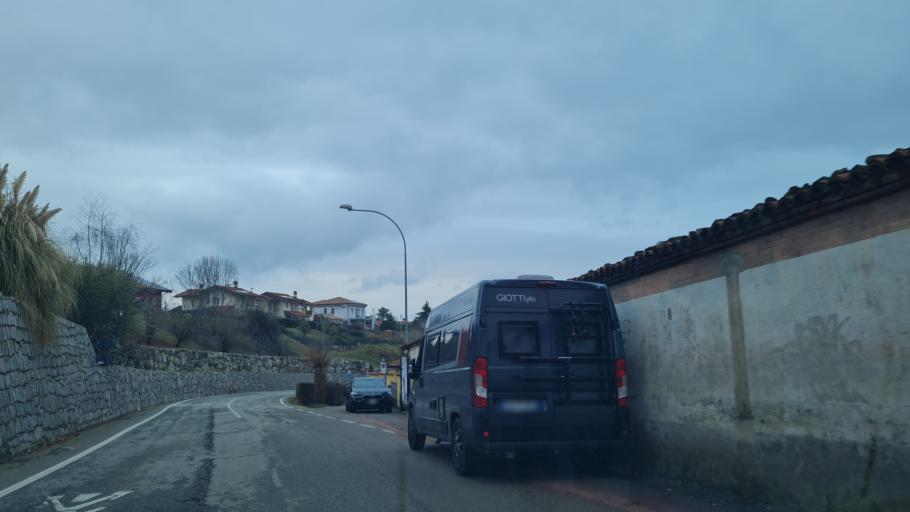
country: IT
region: Piedmont
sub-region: Provincia di Biella
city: Muzzano
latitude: 45.5689
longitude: 7.9840
